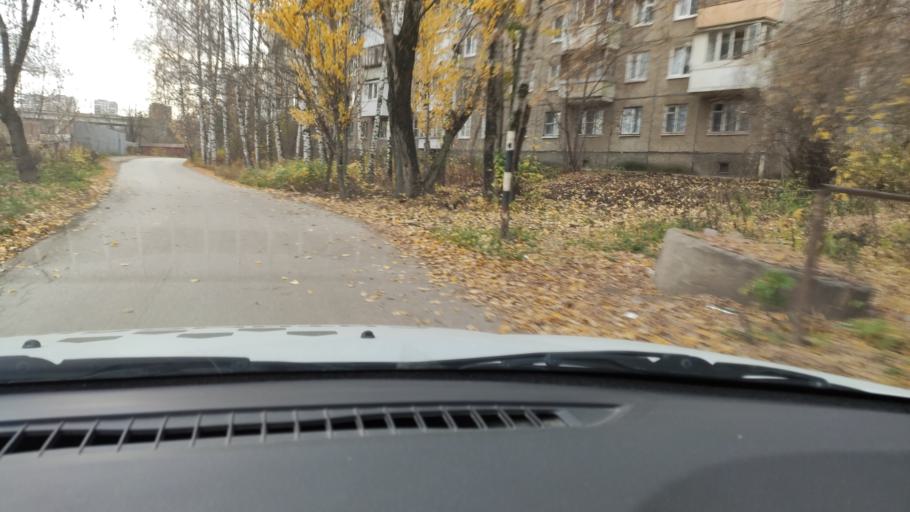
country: RU
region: Perm
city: Perm
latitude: 57.9888
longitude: 56.2338
